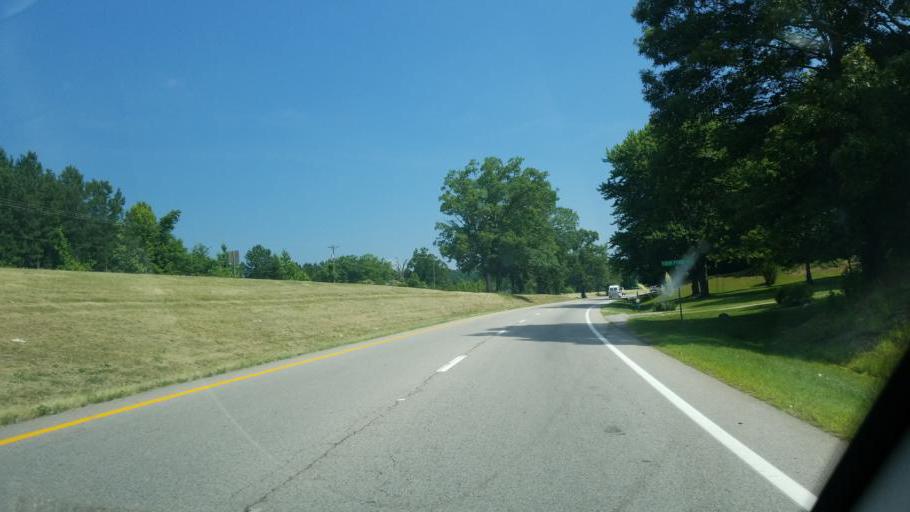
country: US
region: Virginia
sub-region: Pittsylvania County
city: Mount Hermon
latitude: 36.7239
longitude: -79.3849
